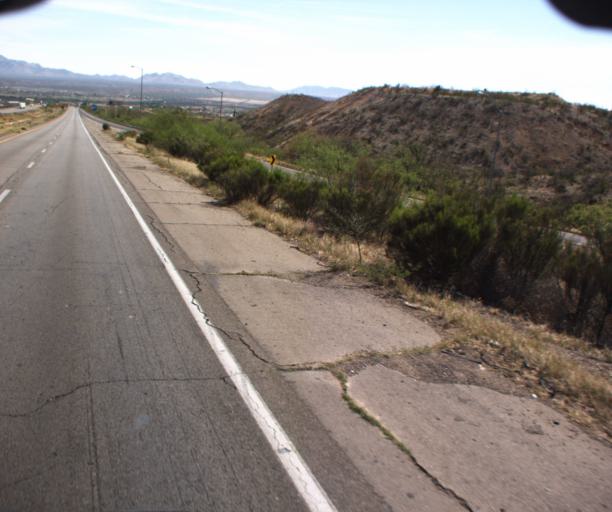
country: US
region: Arizona
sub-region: Cochise County
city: Whetstone
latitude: 31.9733
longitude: -110.3230
